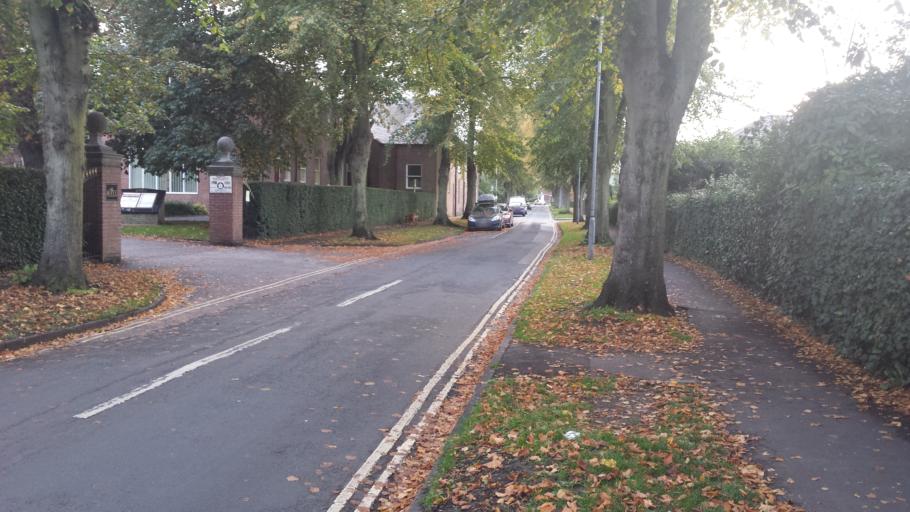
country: GB
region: England
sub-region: East Riding of Yorkshire
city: Beverley
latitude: 53.8401
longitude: -0.4315
